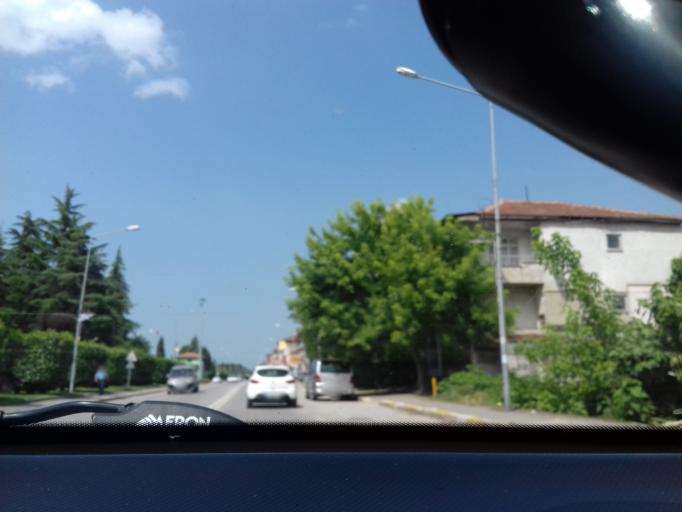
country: TR
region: Sakarya
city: Adapazari
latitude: 40.7216
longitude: 30.3698
